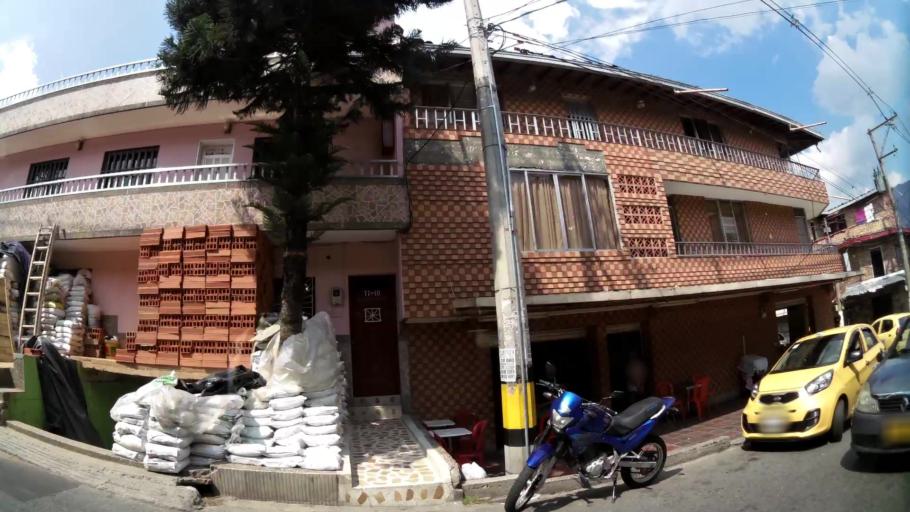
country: CO
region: Antioquia
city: Medellin
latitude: 6.2883
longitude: -75.5759
